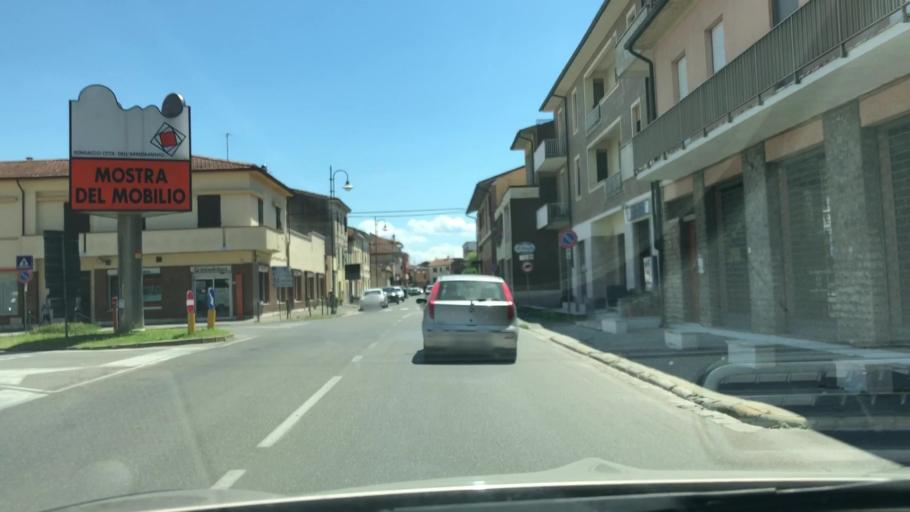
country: IT
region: Tuscany
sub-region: Province of Pisa
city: Ponsacco
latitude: 43.6238
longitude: 10.6298
